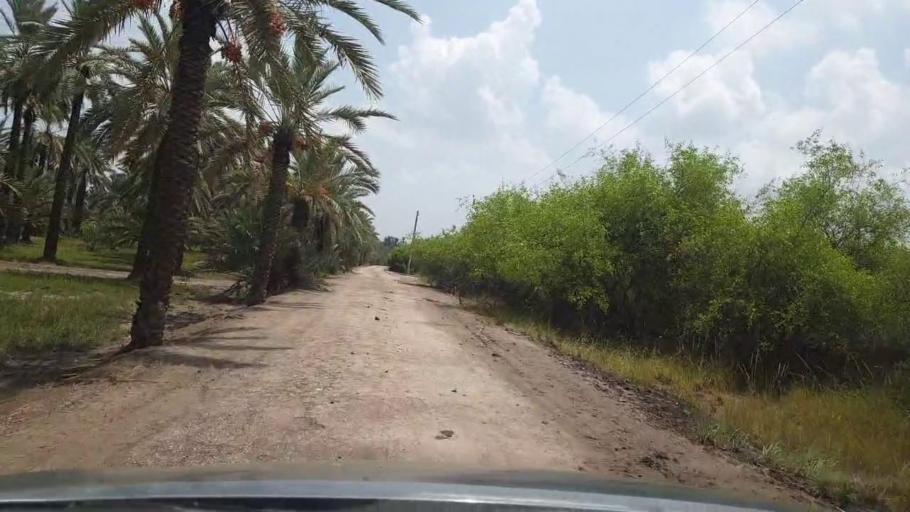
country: PK
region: Sindh
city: Khairpur
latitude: 27.6358
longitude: 68.7274
